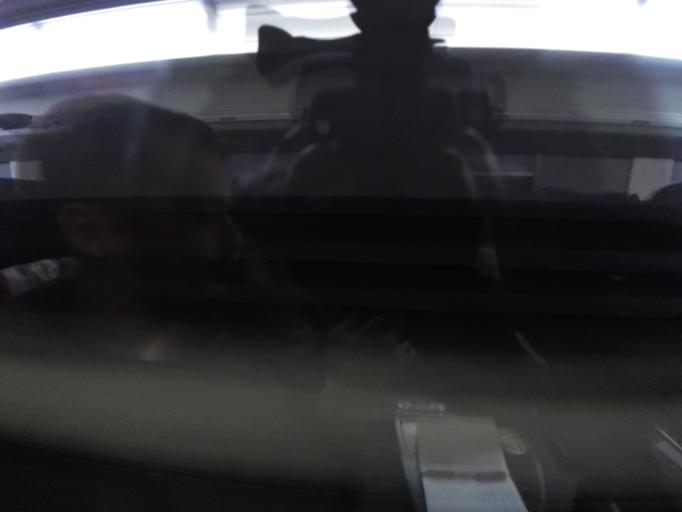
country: KR
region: Chungcheongbuk-do
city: Okcheon
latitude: 36.2461
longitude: 127.6317
